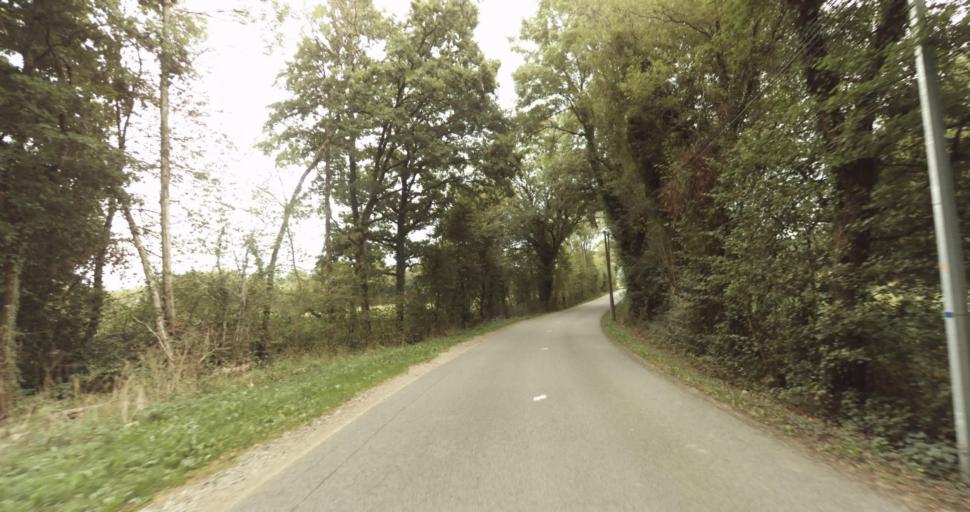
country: FR
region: Lower Normandy
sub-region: Departement de l'Orne
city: Gace
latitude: 48.6902
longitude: 0.2682
